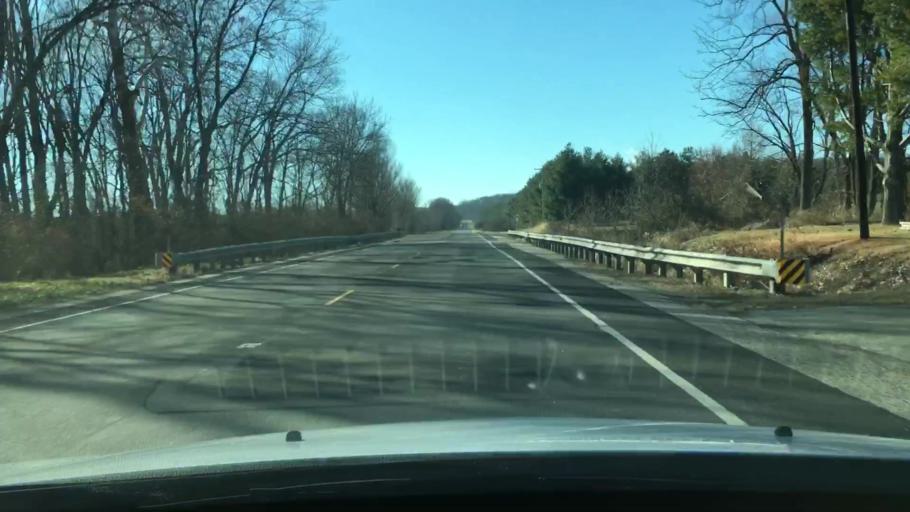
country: US
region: Illinois
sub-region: Fulton County
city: Canton
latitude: 40.4959
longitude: -89.9350
